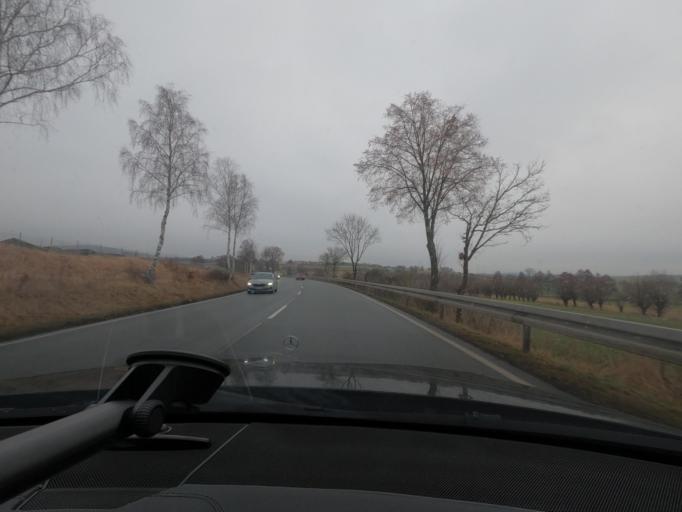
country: DE
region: Hesse
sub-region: Regierungsbezirk Kassel
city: Wolfhagen
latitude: 51.3337
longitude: 9.1456
